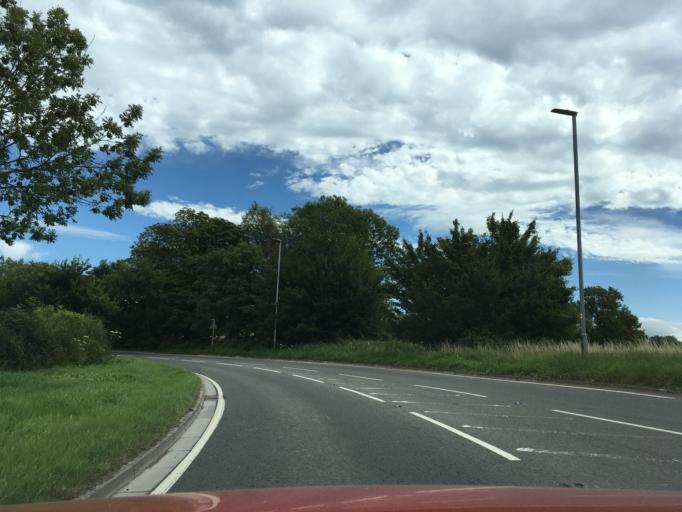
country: GB
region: England
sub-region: Somerset
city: Cheddar
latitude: 51.2696
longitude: -2.7725
